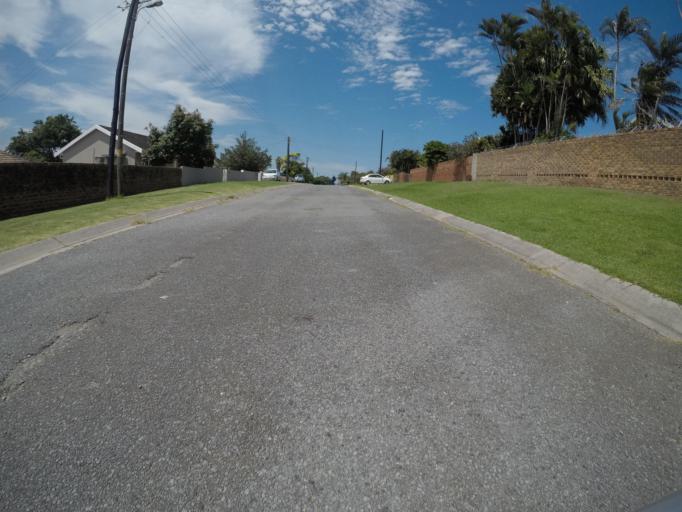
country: ZA
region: Eastern Cape
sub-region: Buffalo City Metropolitan Municipality
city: East London
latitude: -33.0313
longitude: 27.8641
